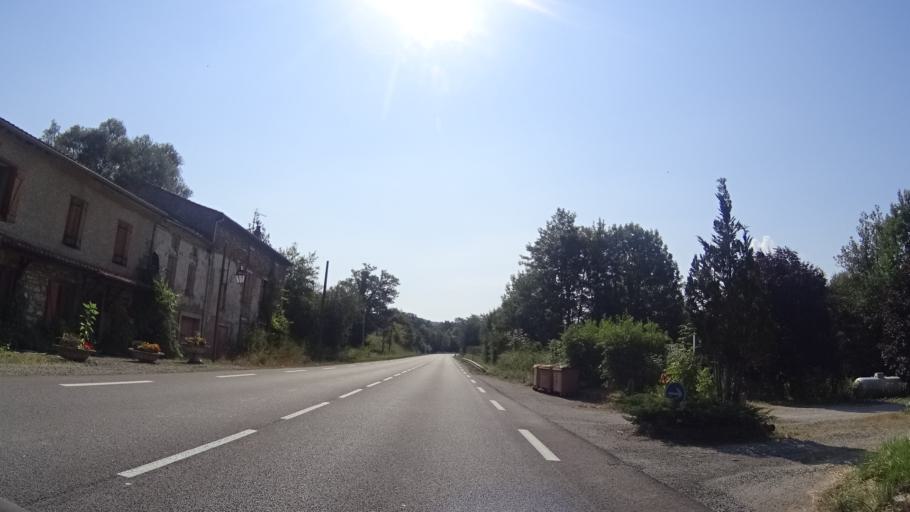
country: FR
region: Midi-Pyrenees
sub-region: Departement de l'Ariege
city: Saint-Paul-de-Jarrat
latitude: 42.9276
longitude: 1.7403
